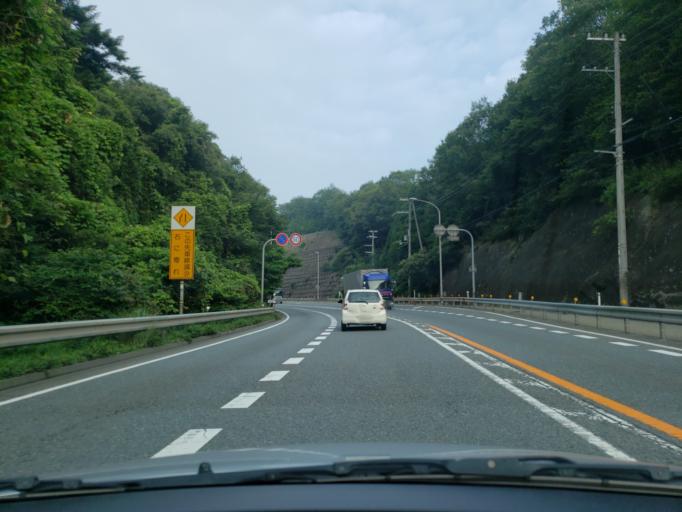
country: JP
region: Hyogo
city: Kariya
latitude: 34.8433
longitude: 134.3283
